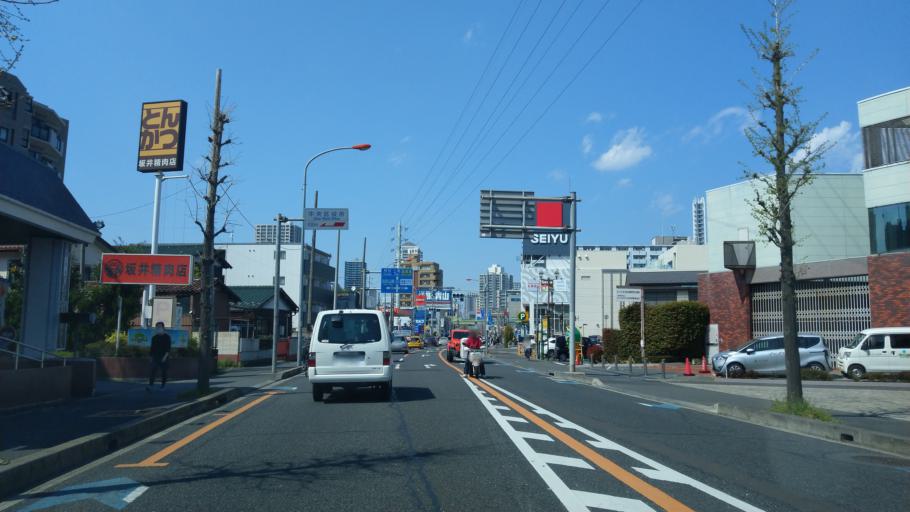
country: JP
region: Saitama
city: Yono
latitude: 35.8833
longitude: 139.6319
